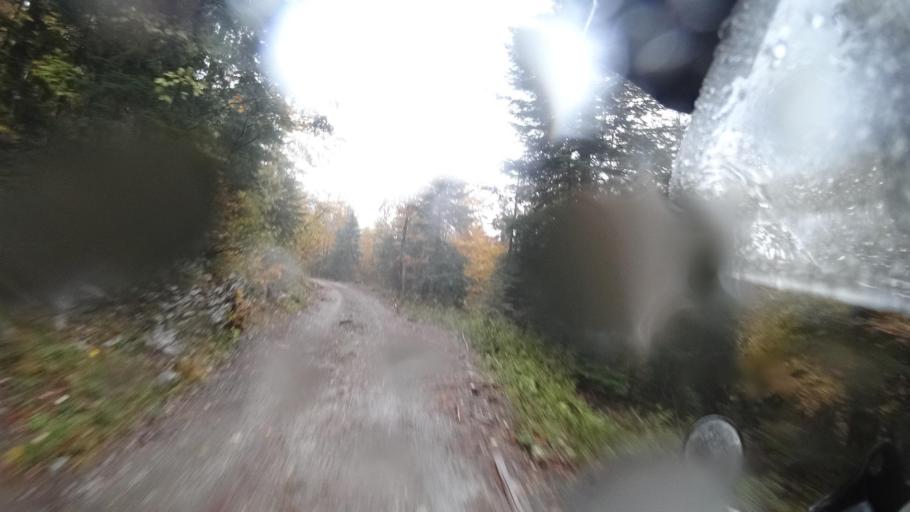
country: HR
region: Primorsko-Goranska
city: Vrbovsko
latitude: 45.2973
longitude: 15.0327
